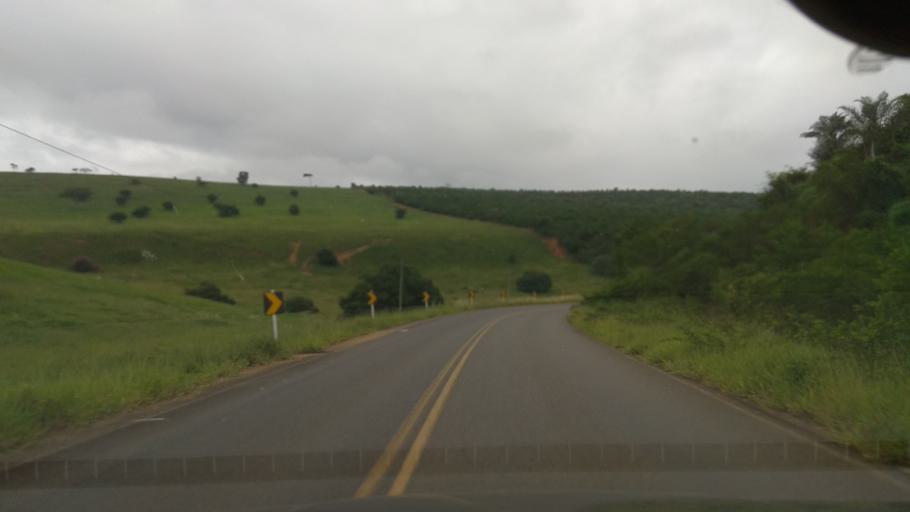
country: BR
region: Bahia
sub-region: Santa Ines
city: Santa Ines
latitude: -13.2537
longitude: -39.7832
